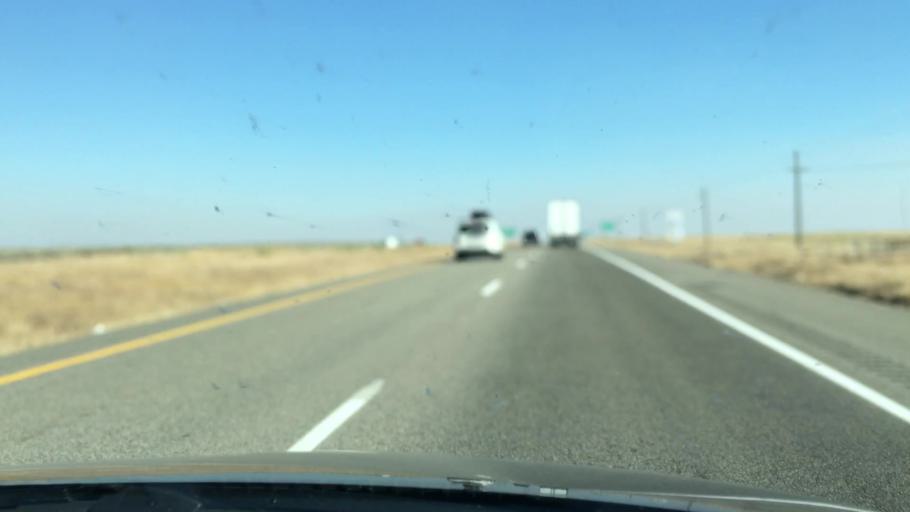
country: US
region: Idaho
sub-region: Ada County
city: Boise
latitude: 43.4555
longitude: -116.0842
